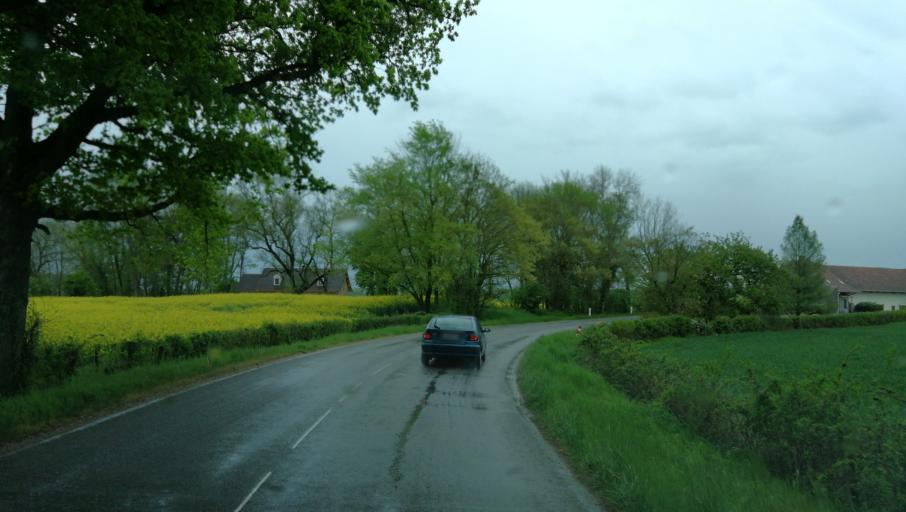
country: FR
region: Bourgogne
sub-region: Departement de Saone-et-Loire
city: Pierre-de-Bresse
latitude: 46.8975
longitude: 5.2583
